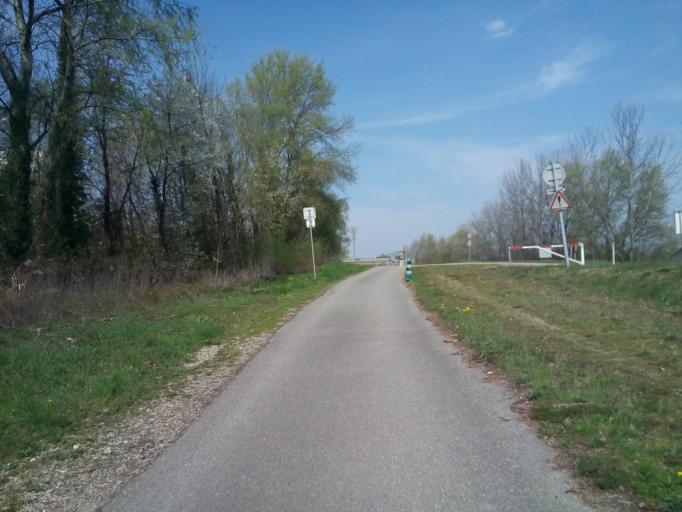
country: FR
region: Alsace
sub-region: Departement du Bas-Rhin
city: Seltz
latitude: 48.8568
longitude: 8.1077
